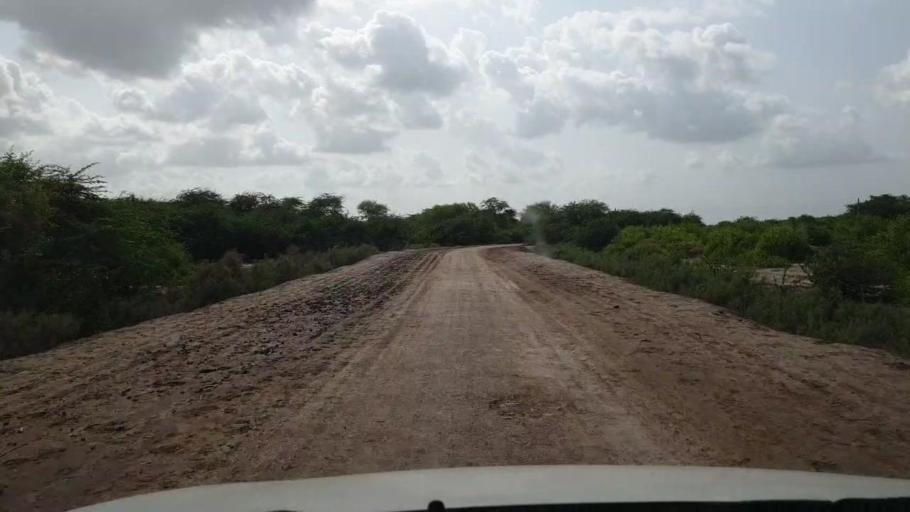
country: PK
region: Sindh
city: Kario
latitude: 24.7156
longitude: 68.6388
